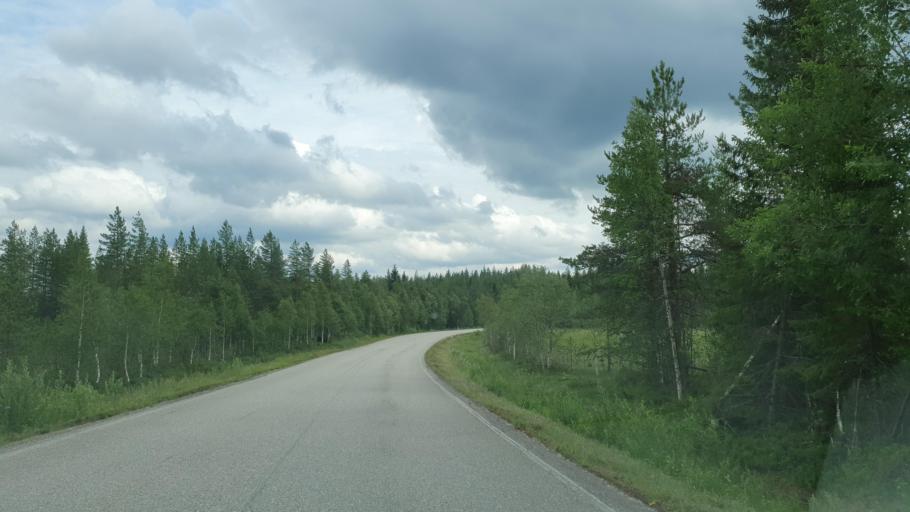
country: FI
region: Kainuu
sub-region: Kehys-Kainuu
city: Kuhmo
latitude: 64.5971
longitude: 29.8074
